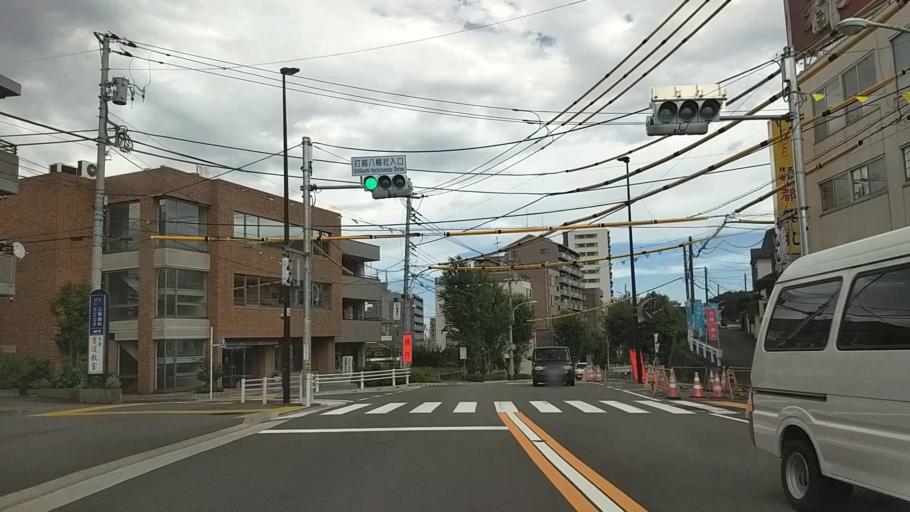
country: JP
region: Tokyo
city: Hachioji
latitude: 35.6443
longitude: 139.3496
